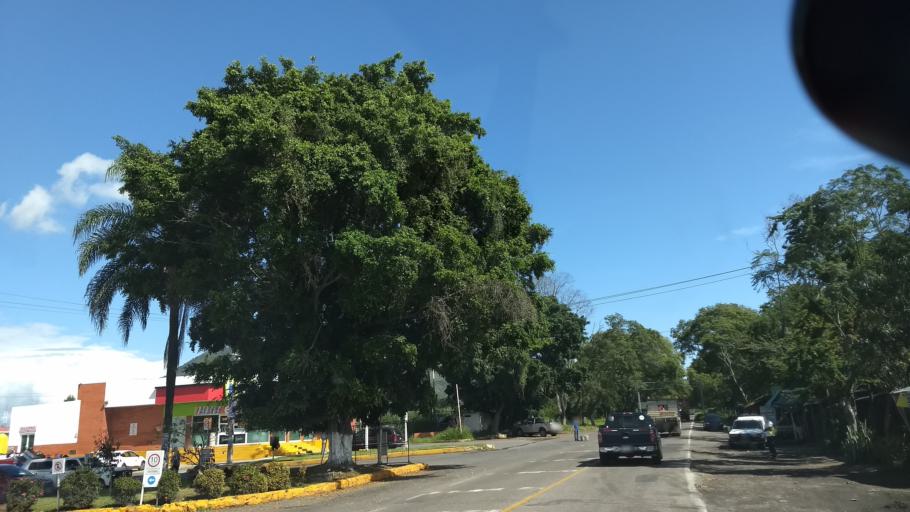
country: MX
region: Jalisco
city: Tuxpan
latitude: 19.5301
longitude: -103.4210
